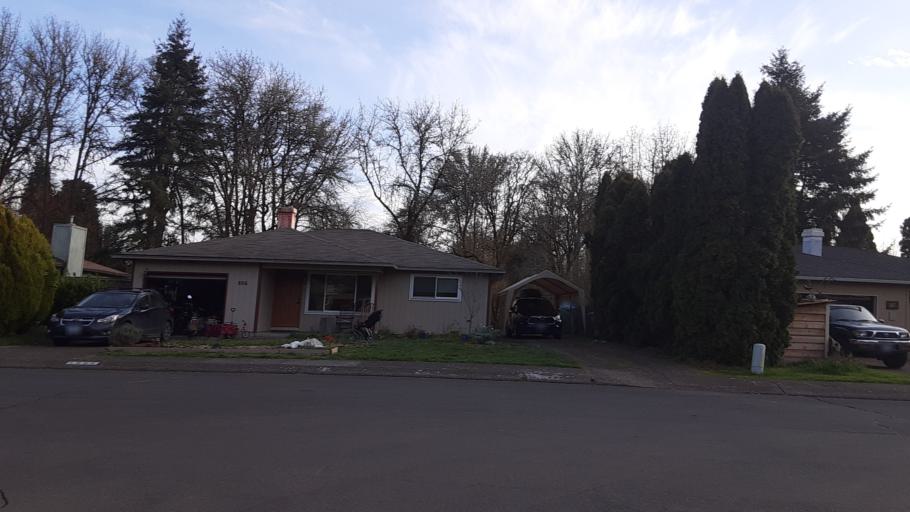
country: US
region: Oregon
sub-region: Benton County
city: Corvallis
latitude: 44.5462
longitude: -123.2584
